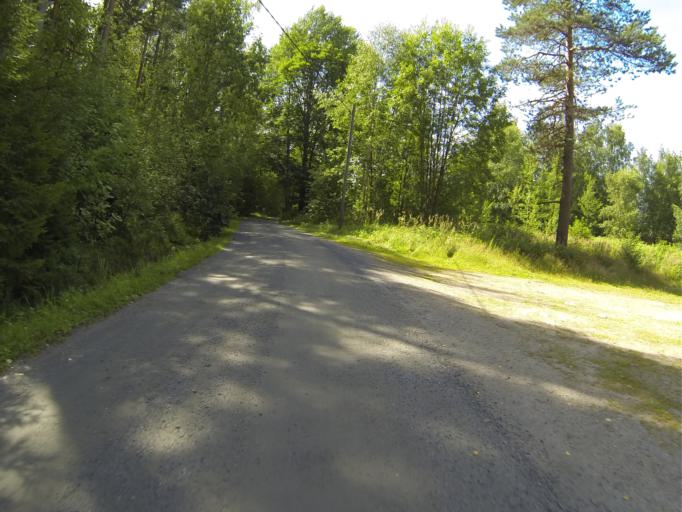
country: FI
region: Varsinais-Suomi
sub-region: Salo
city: Halikko
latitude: 60.2746
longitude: 22.9957
